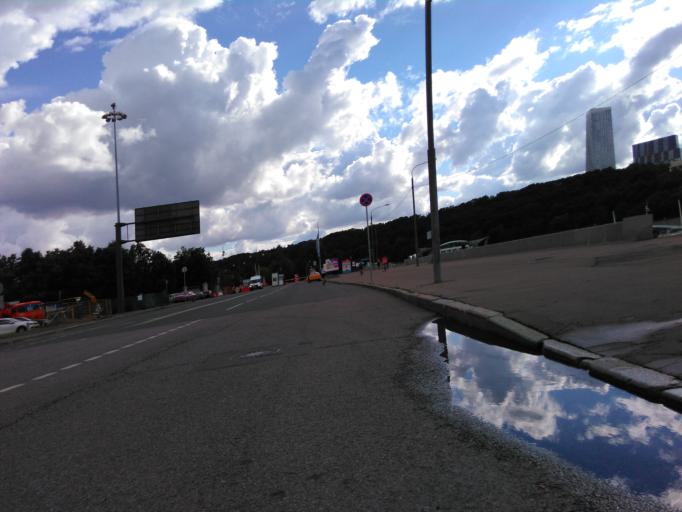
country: RU
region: Moscow
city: Luzhniki
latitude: 55.7269
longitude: 37.5468
